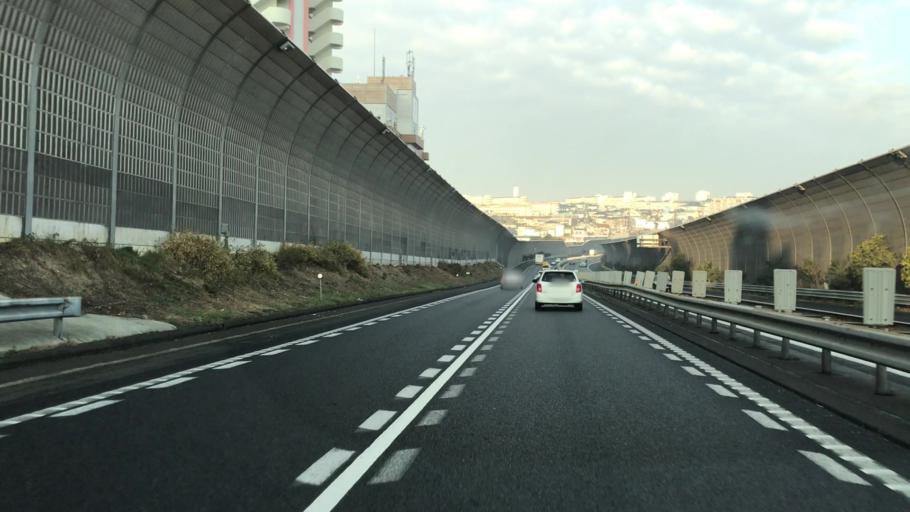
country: JP
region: Hyogo
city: Akashi
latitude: 34.6508
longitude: 135.0424
